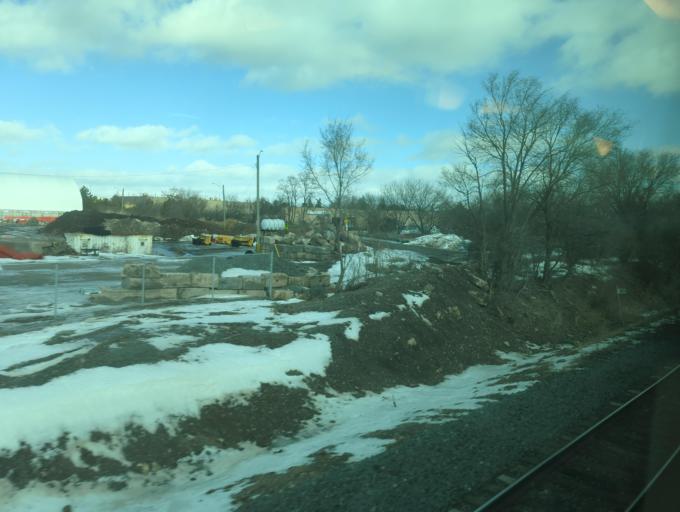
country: CA
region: Ontario
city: Burlington
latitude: 43.3552
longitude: -79.7868
